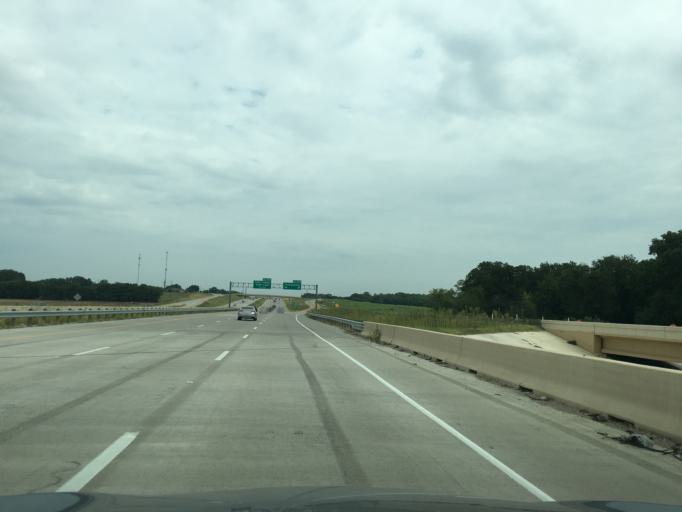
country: US
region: Texas
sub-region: Collin County
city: Melissa
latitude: 33.3010
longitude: -96.5913
